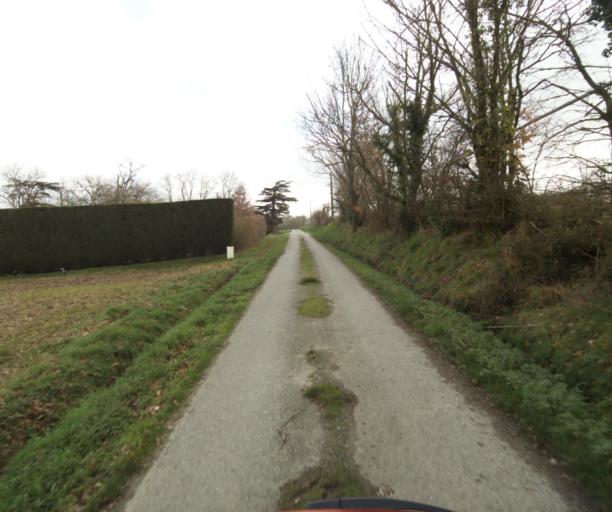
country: FR
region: Midi-Pyrenees
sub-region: Departement de l'Ariege
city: Mazeres
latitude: 43.2300
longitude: 1.7124
